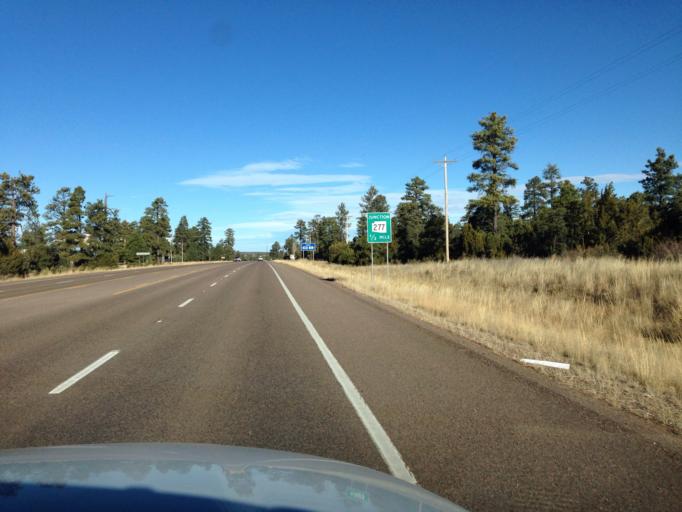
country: US
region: Arizona
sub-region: Navajo County
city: Heber-Overgaard
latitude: 34.4101
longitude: -110.5693
